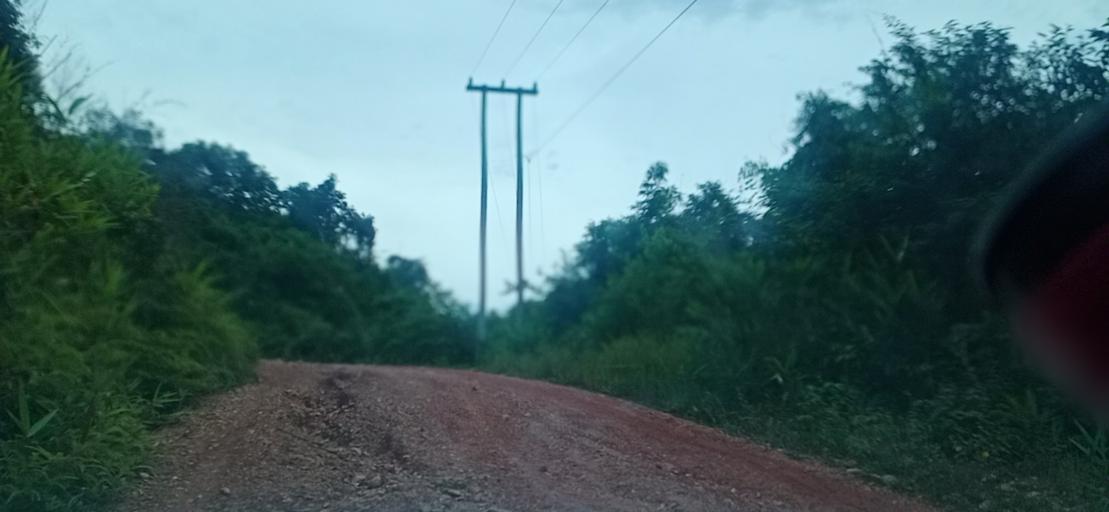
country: TH
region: Changwat Bueng Kan
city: Pak Khat
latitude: 18.5597
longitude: 103.2497
